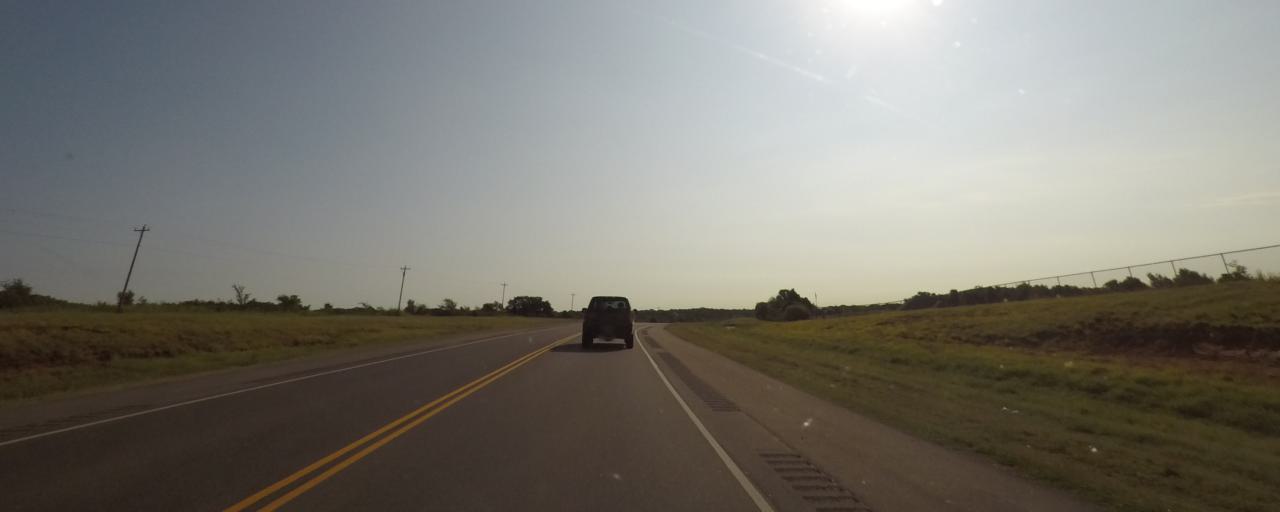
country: US
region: Oklahoma
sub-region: McClain County
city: Blanchard
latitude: 35.1236
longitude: -97.6992
